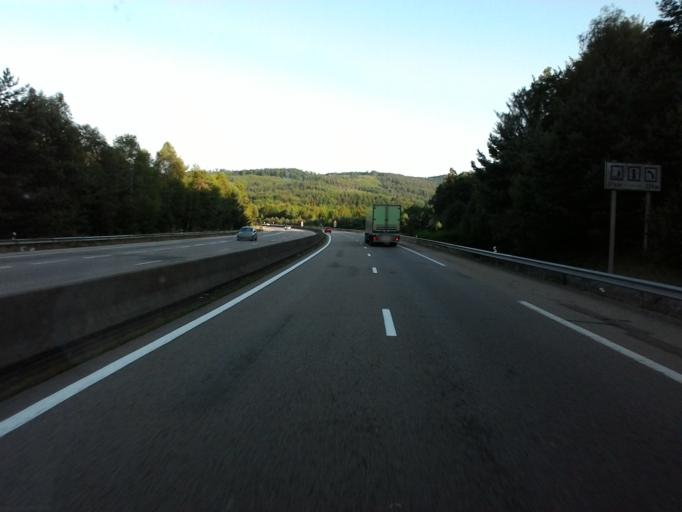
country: FR
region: Lorraine
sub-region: Departement des Vosges
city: Epinal
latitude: 48.1520
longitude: 6.4861
